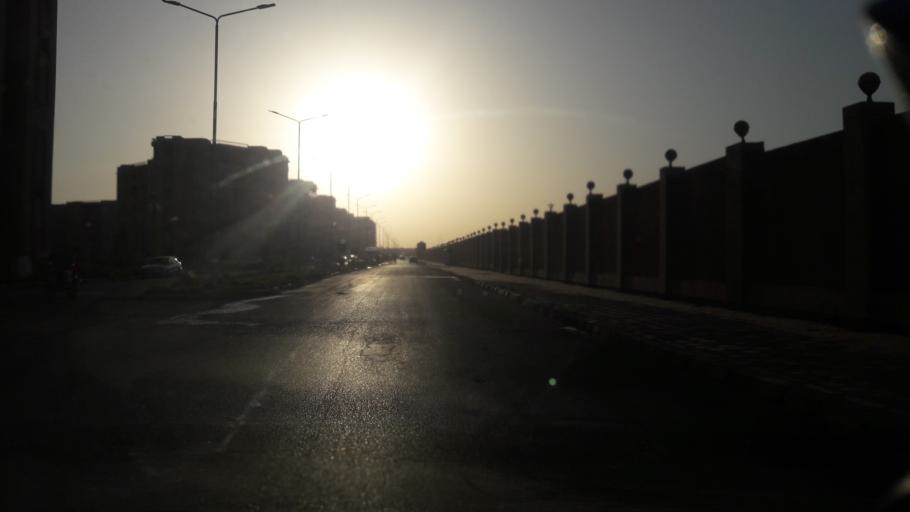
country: EG
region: Al Jizah
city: Madinat Sittah Uktubar
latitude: 29.9579
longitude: 31.0445
